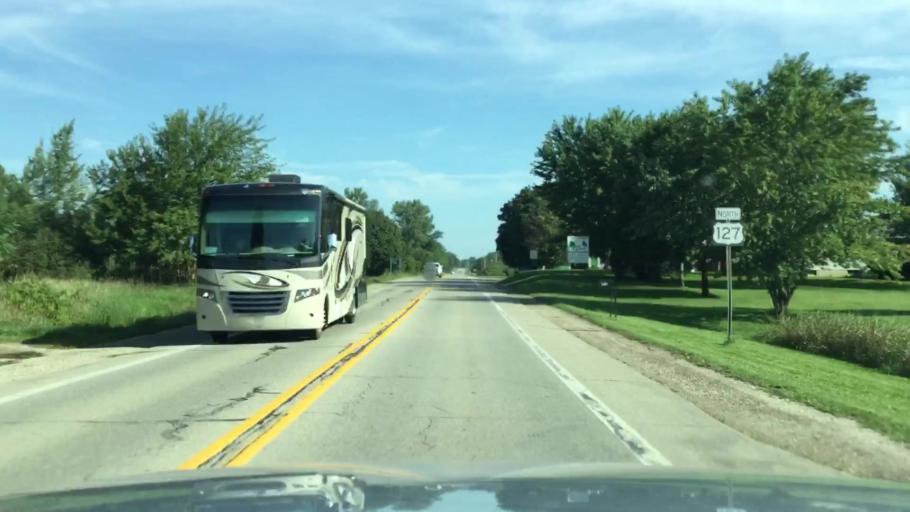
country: US
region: Michigan
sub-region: Lenawee County
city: Manitou Beach-Devils Lake
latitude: 41.9427
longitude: -84.3671
